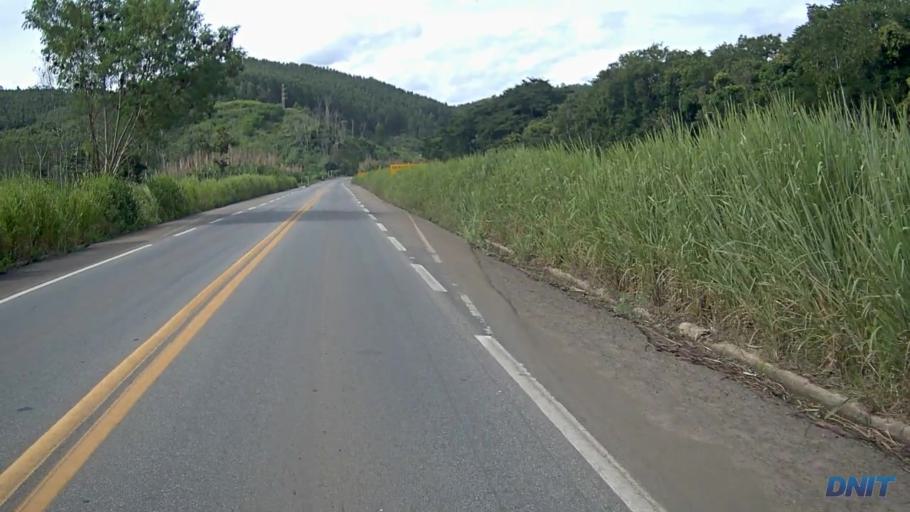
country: BR
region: Minas Gerais
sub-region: Ipaba
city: Ipaba
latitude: -19.3644
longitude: -42.4490
